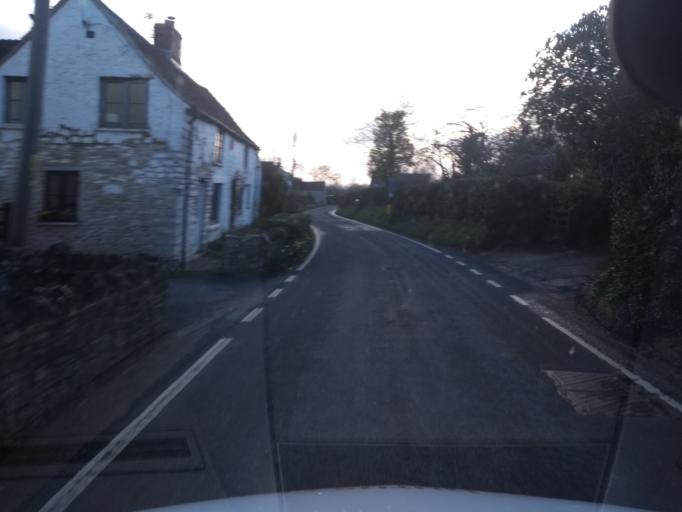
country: GB
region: England
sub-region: Somerset
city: Wedmore
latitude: 51.2251
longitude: -2.8002
